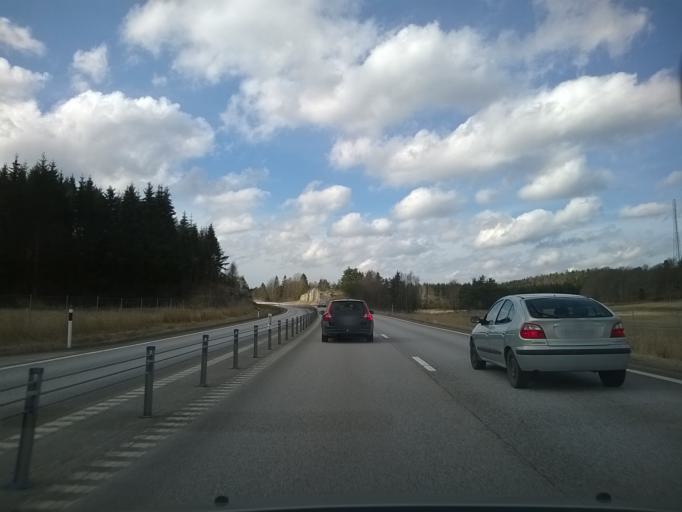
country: SE
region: Vaestra Goetaland
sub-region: Orust
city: Henan
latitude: 58.3510
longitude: 11.7390
